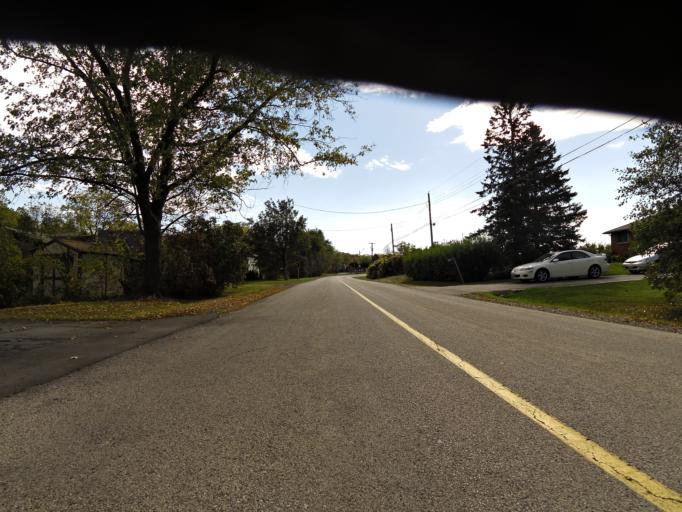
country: CA
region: Ontario
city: Ancaster
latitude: 43.2975
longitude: -79.9335
